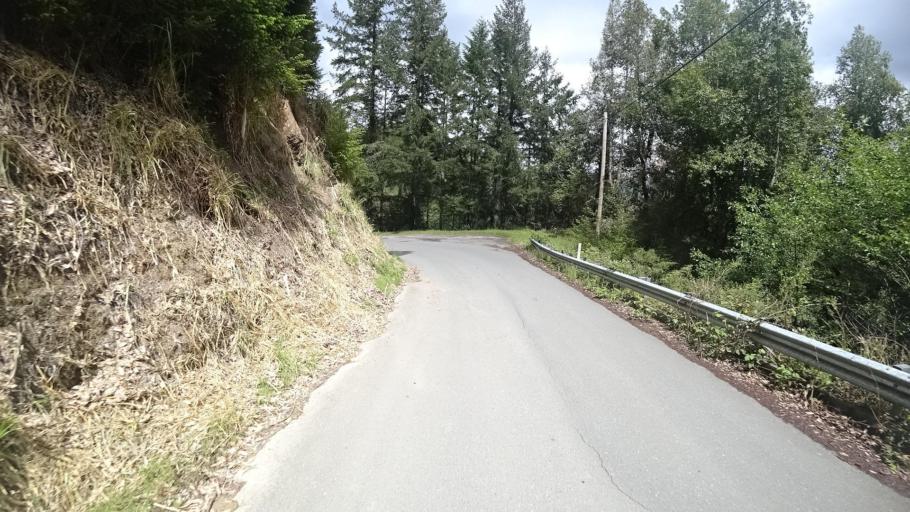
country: US
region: California
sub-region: Humboldt County
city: Blue Lake
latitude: 40.7592
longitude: -123.9132
